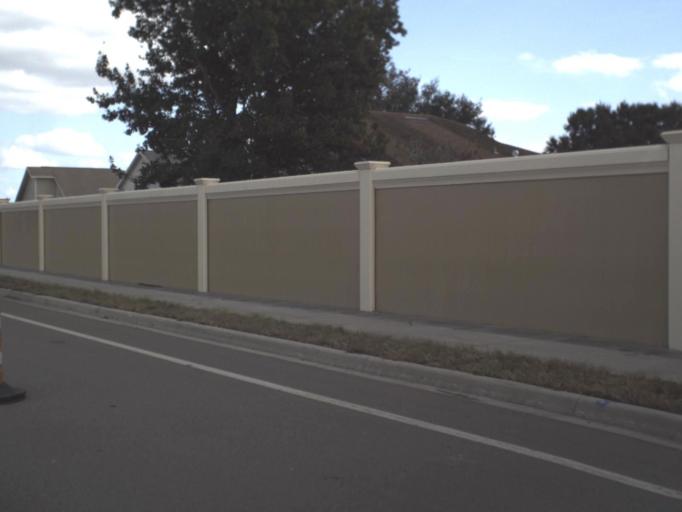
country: US
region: Florida
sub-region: Osceola County
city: Buenaventura Lakes
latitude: 28.3454
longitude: -81.3694
